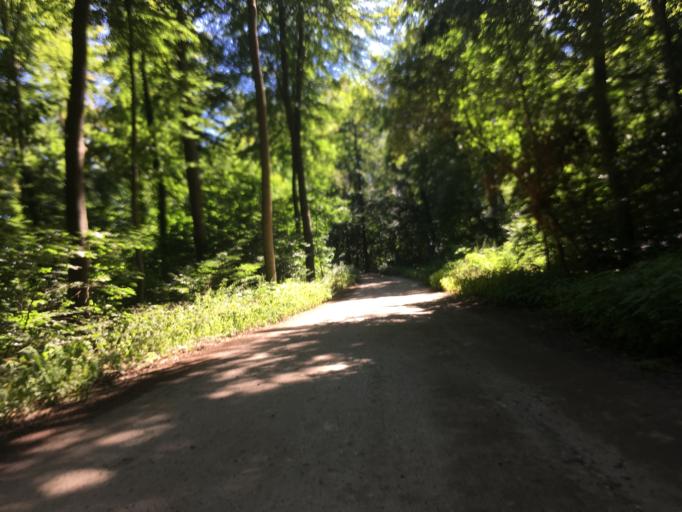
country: DE
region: Brandenburg
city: Grosswoltersdorf
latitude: 53.1499
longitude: 13.0447
